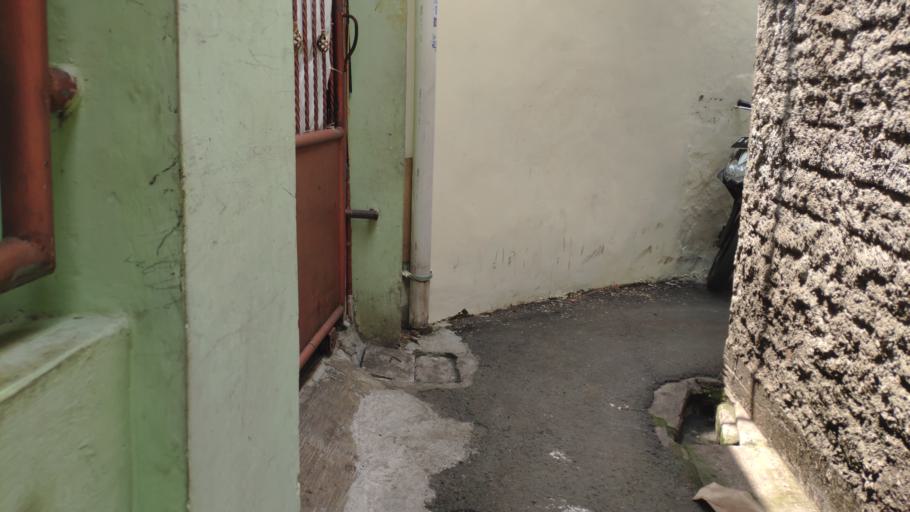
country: ID
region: Jakarta Raya
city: Jakarta
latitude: -6.2126
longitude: 106.8717
